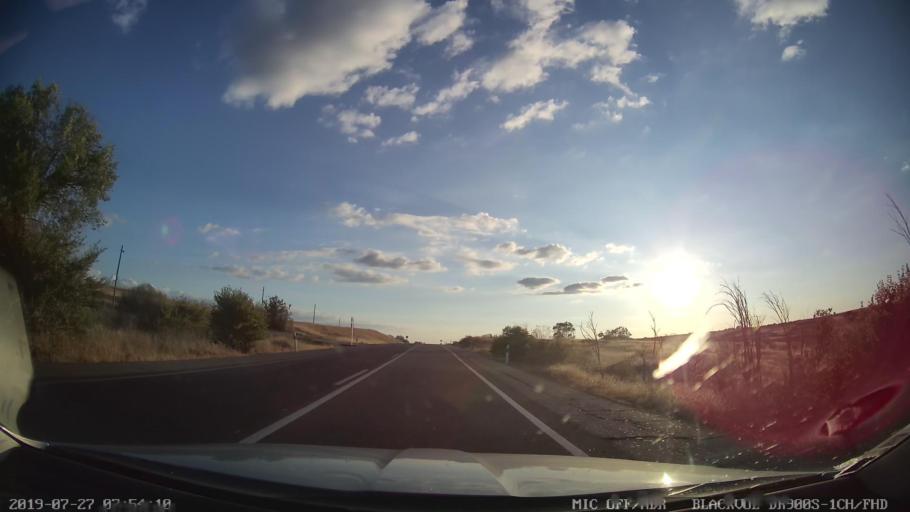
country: ES
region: Extremadura
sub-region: Provincia de Badajoz
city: Trujillanos
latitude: 38.9404
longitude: -6.2950
